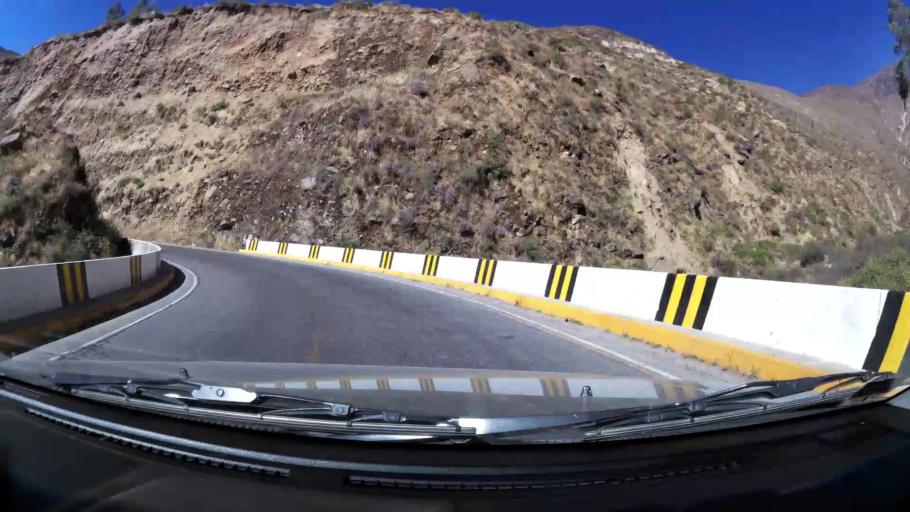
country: PE
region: Huancavelica
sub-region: Huaytara
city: Quito-Arma
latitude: -13.6081
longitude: -75.3349
